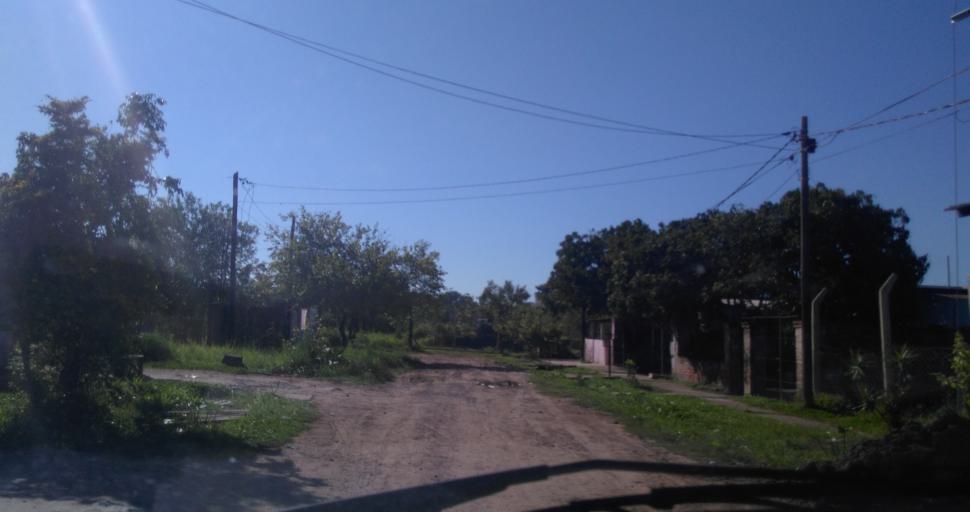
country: AR
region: Chaco
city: Resistencia
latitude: -27.4392
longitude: -58.9626
